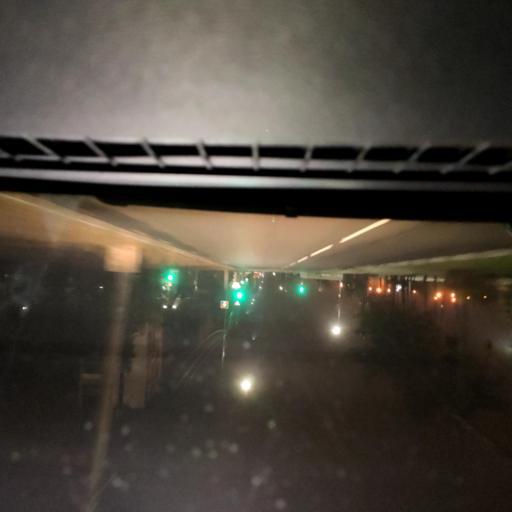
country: RU
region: Voronezj
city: Voronezh
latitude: 51.6528
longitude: 39.1354
